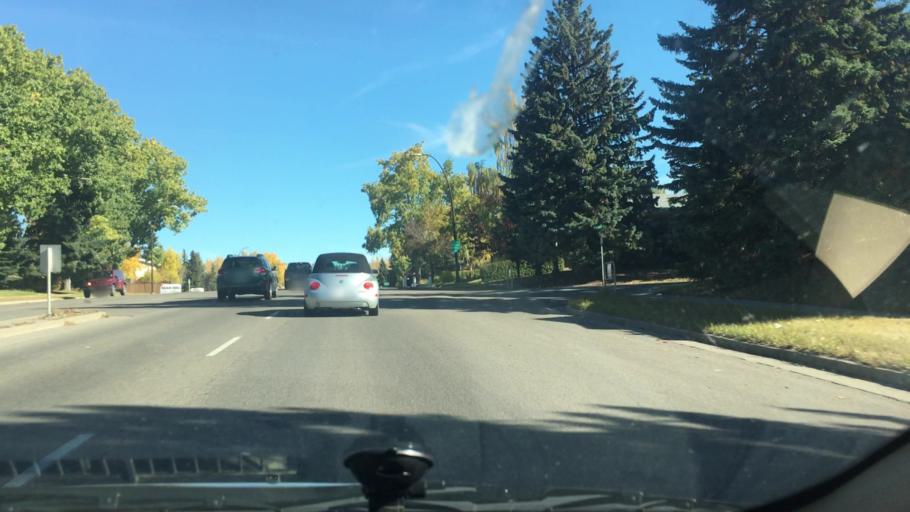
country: CA
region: Alberta
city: Calgary
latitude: 51.1084
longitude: -114.1615
